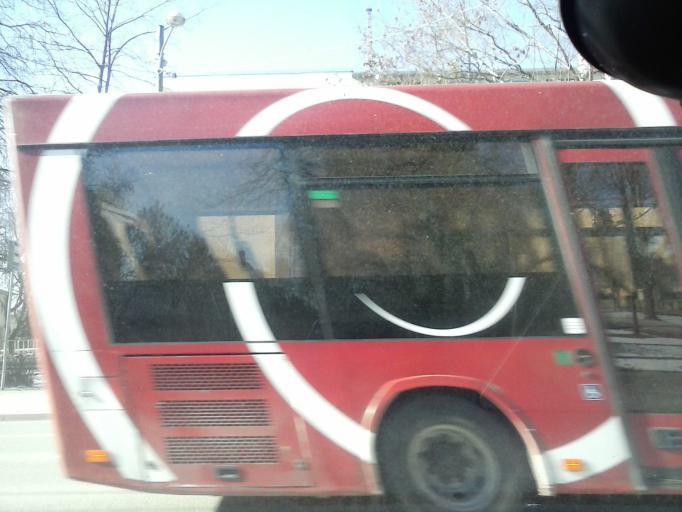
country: EE
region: Tartu
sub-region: Tartu linn
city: Tartu
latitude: 58.3637
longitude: 26.7070
